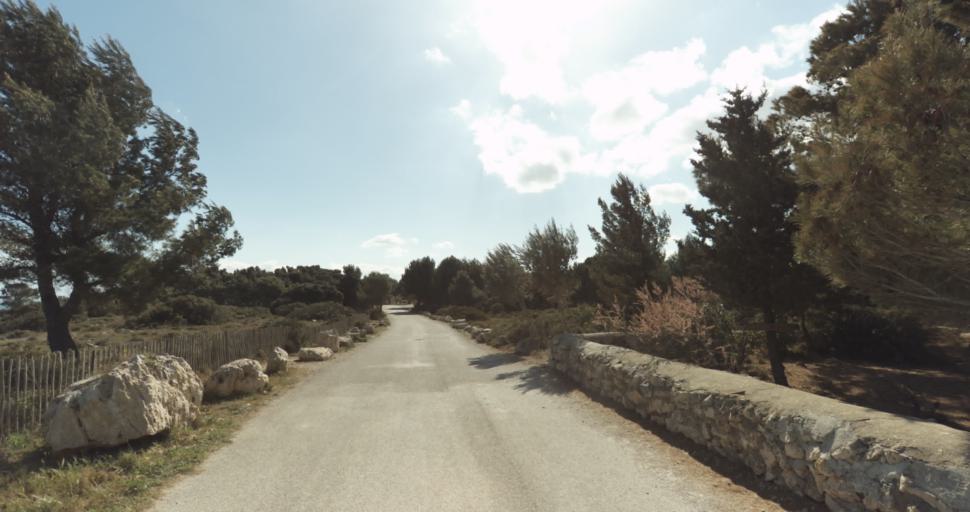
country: FR
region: Languedoc-Roussillon
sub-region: Departement de l'Aude
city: Leucate
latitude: 42.9100
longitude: 3.0560
